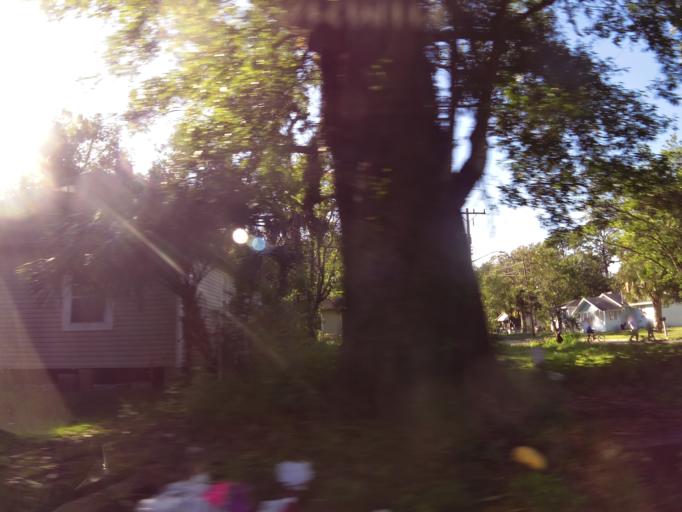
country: US
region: Florida
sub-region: Duval County
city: Jacksonville
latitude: 30.3558
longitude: -81.6847
